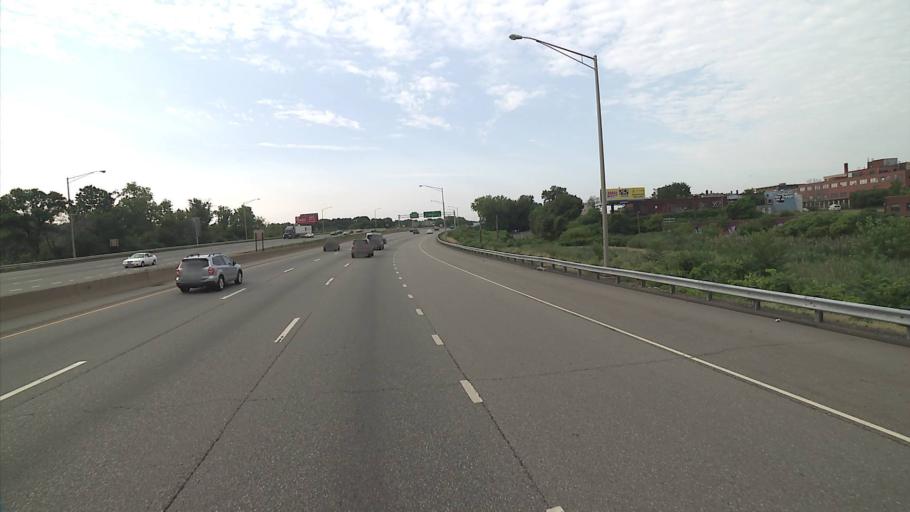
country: US
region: Connecticut
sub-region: Hartford County
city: Hartford
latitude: 41.7557
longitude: -72.7009
